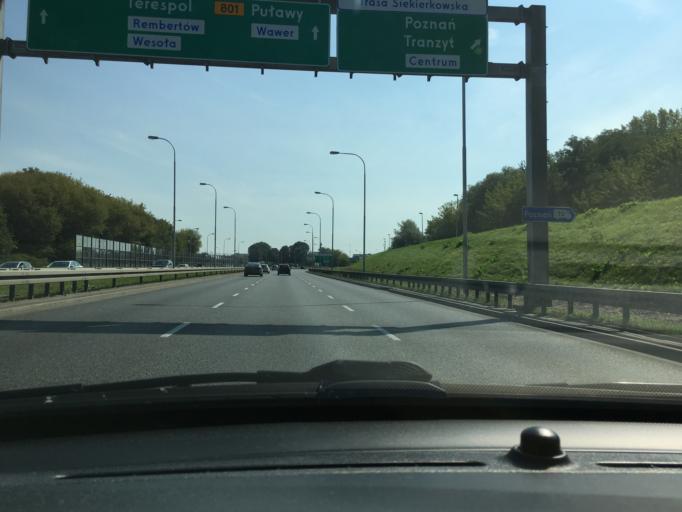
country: PL
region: Masovian Voivodeship
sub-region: Warszawa
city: Praga Poludnie
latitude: 52.2196
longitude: 21.0907
